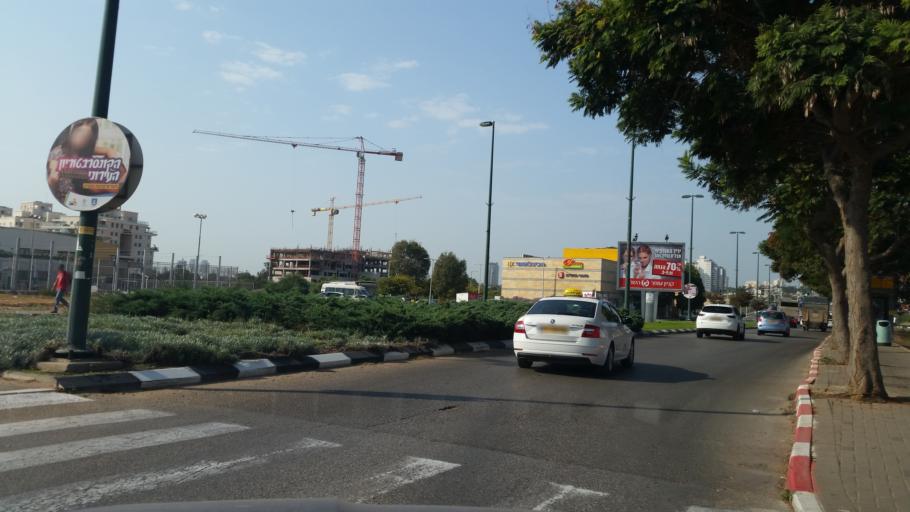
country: IL
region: Central District
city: Bet Yizhaq
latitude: 32.3124
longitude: 34.8722
